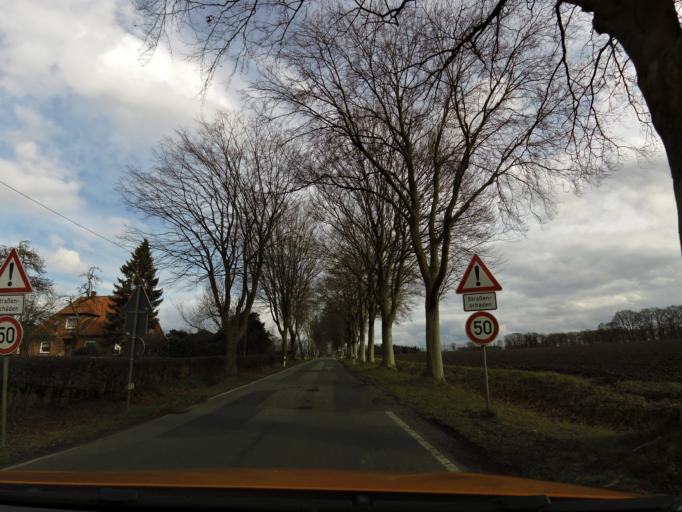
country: DE
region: Lower Saxony
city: Wildeshausen
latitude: 52.9369
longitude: 8.4637
